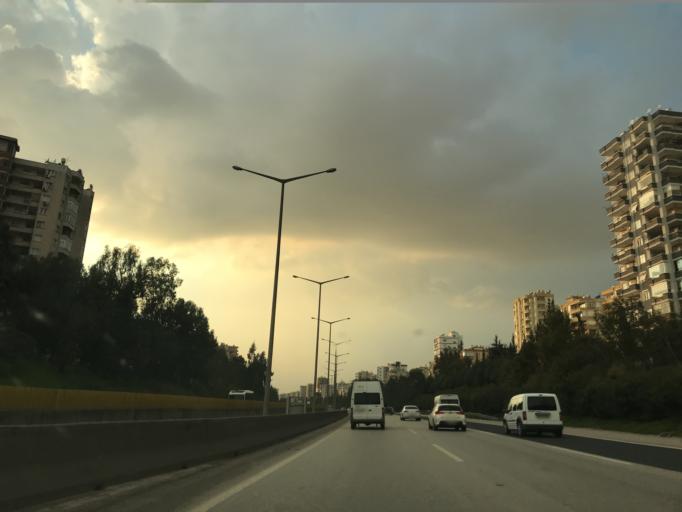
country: TR
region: Adana
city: Adana
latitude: 37.0314
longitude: 35.3089
